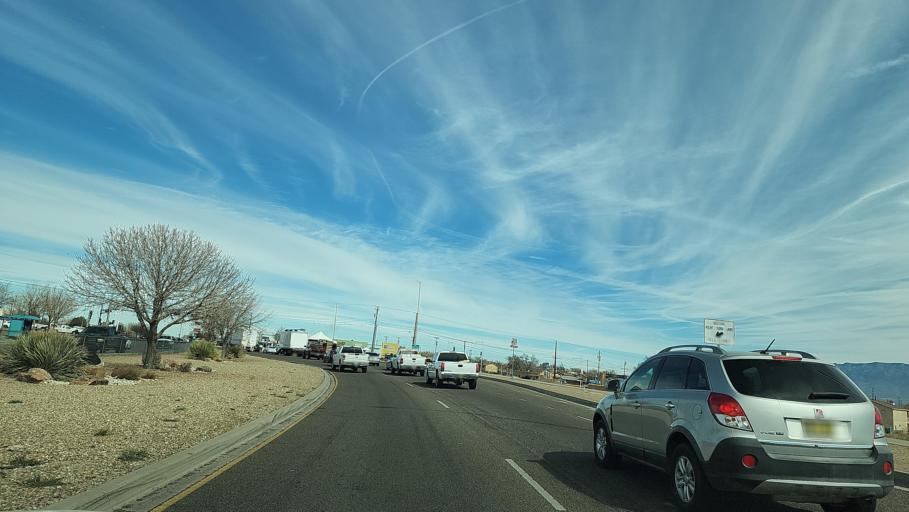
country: US
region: New Mexico
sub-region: Bernalillo County
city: Albuquerque
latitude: 35.0785
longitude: -106.7105
